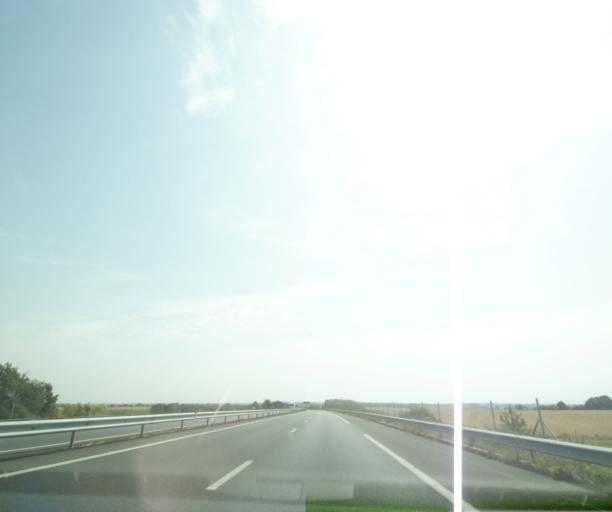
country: FR
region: Pays de la Loire
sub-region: Departement de la Vendee
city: Sainte-Hermine
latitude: 46.5613
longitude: -1.1043
